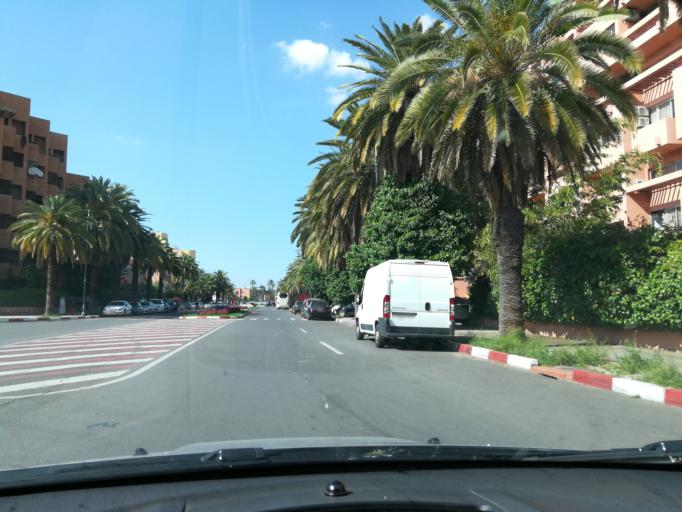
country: MA
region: Marrakech-Tensift-Al Haouz
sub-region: Marrakech
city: Marrakesh
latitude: 31.6268
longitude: -8.0037
